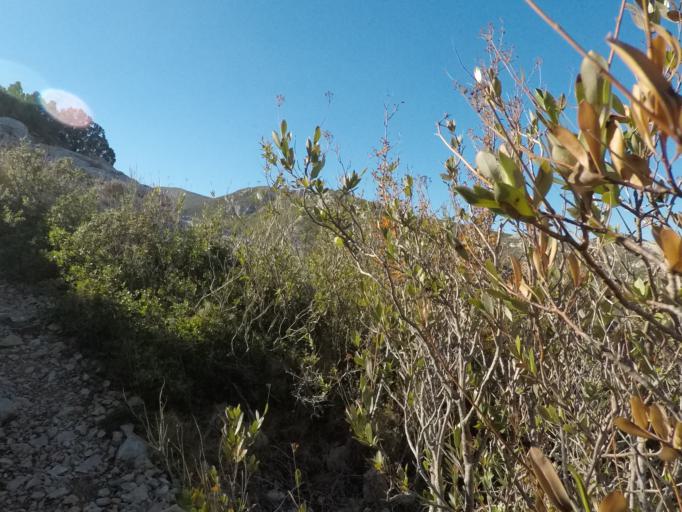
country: FR
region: Provence-Alpes-Cote d'Azur
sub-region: Departement des Bouches-du-Rhone
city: La Penne-sur-Huveaune
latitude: 43.2691
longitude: 5.4901
